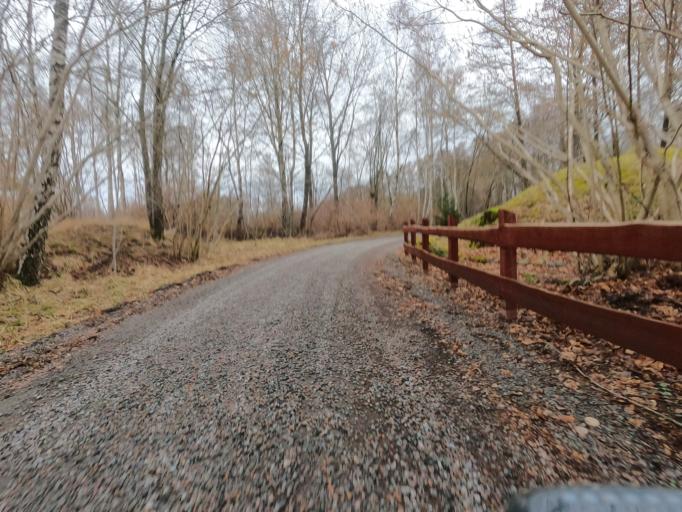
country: SE
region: Kronoberg
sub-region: Ljungby Kommun
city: Ljungby
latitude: 56.8172
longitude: 13.7012
